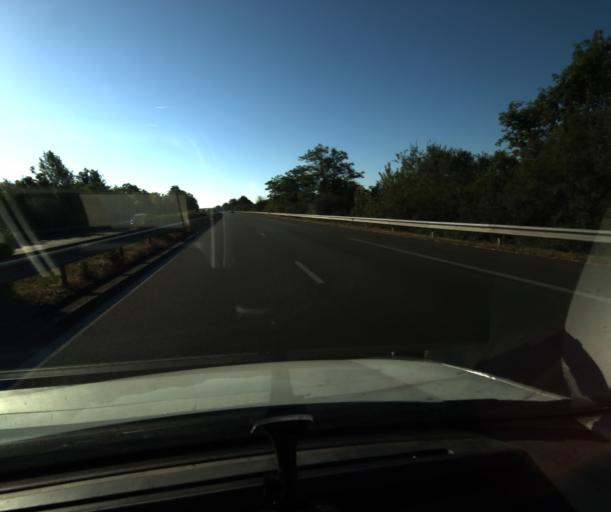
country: FR
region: Midi-Pyrenees
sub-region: Departement du Tarn-et-Garonne
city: Saint-Porquier
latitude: 44.0216
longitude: 1.1753
